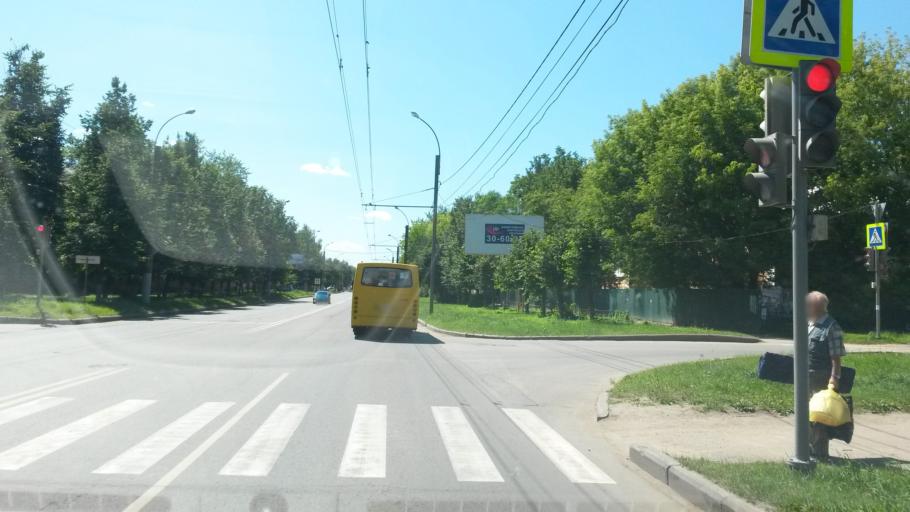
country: RU
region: Ivanovo
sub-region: Gorod Ivanovo
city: Ivanovo
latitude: 56.9806
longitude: 40.9672
